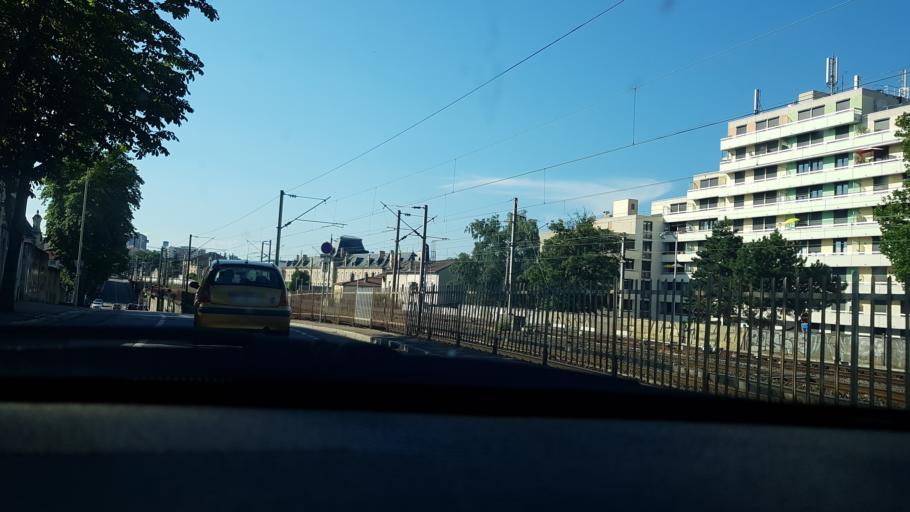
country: FR
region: Lorraine
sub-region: Departement de Meurthe-et-Moselle
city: Nancy
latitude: 48.6783
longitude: 6.1906
